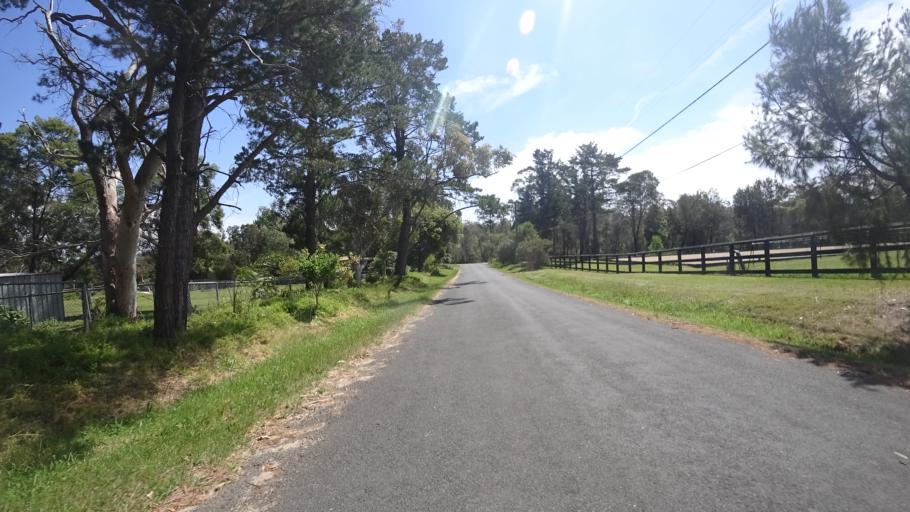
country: AU
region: New South Wales
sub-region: City of Sydney
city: North Turramurra
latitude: -33.6747
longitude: 151.1849
